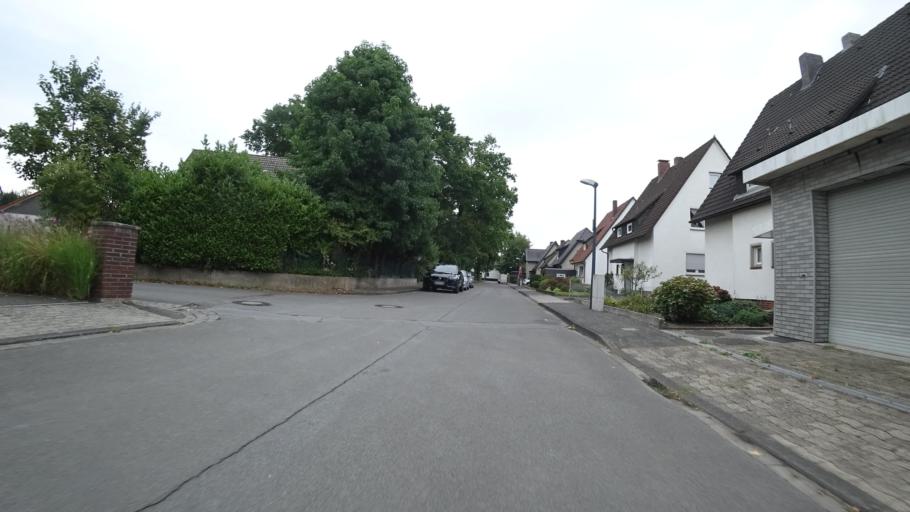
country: DE
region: North Rhine-Westphalia
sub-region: Regierungsbezirk Detmold
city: Guetersloh
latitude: 51.9159
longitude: 8.4156
